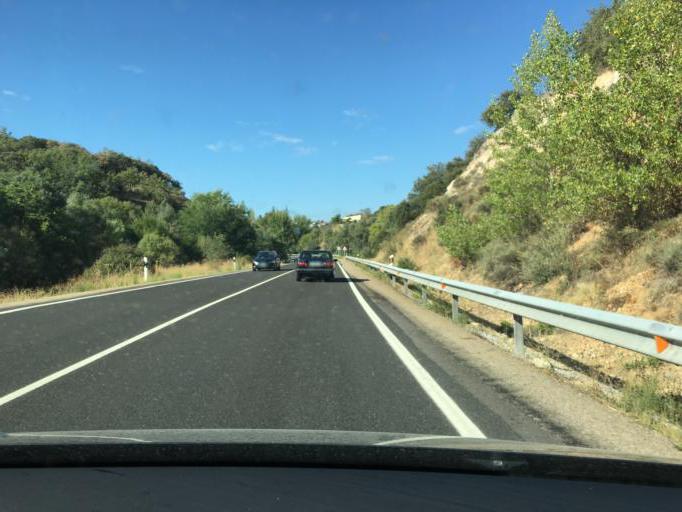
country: ES
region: Madrid
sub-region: Provincia de Madrid
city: Reduena
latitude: 40.8062
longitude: -3.6016
